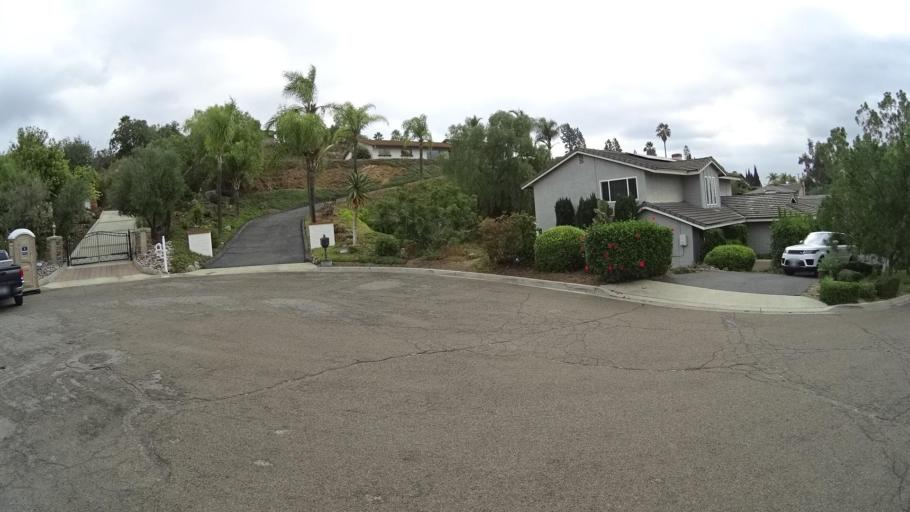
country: US
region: California
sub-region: San Diego County
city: Spring Valley
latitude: 32.7547
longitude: -116.9964
